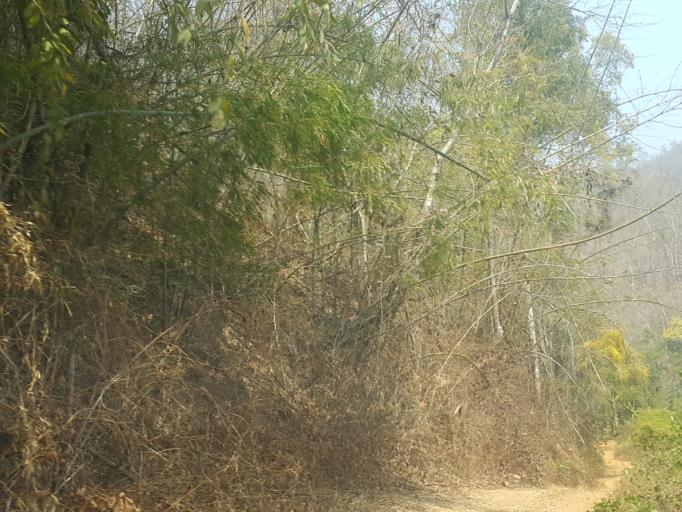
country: TH
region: Chiang Mai
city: Hang Dong
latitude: 18.7532
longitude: 98.8272
